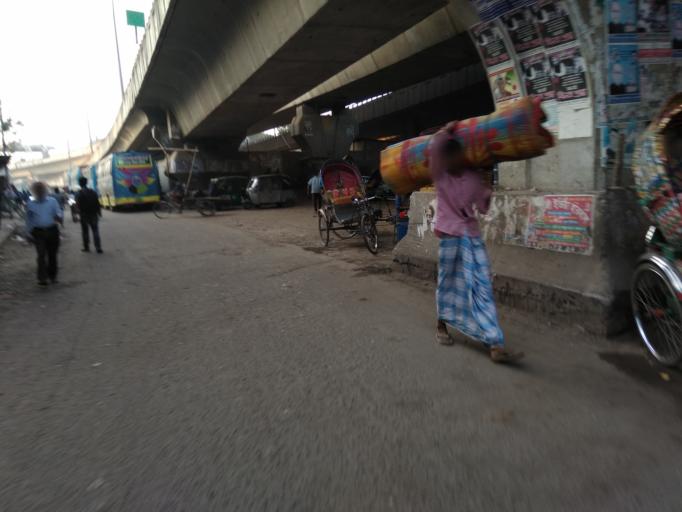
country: BD
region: Dhaka
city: Paltan
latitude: 23.7223
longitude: 90.4155
